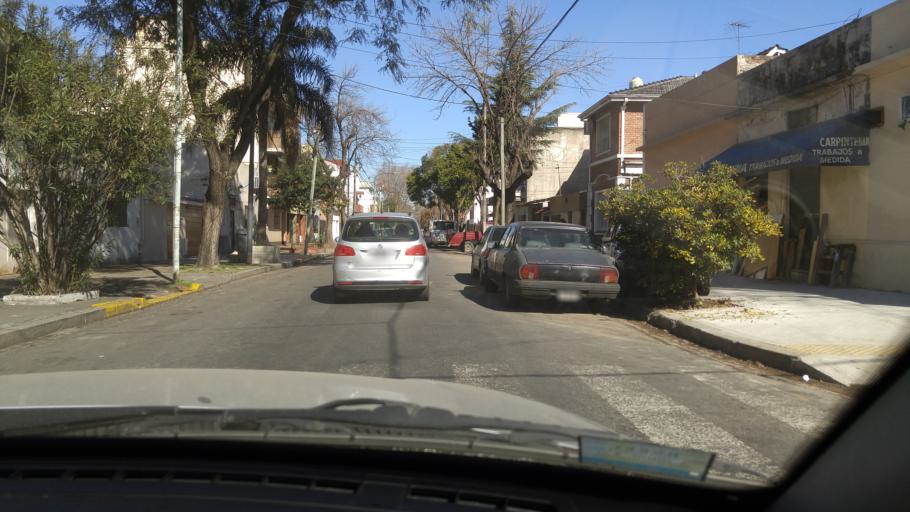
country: AR
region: Buenos Aires F.D.
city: Villa Santa Rita
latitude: -34.6315
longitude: -58.5062
